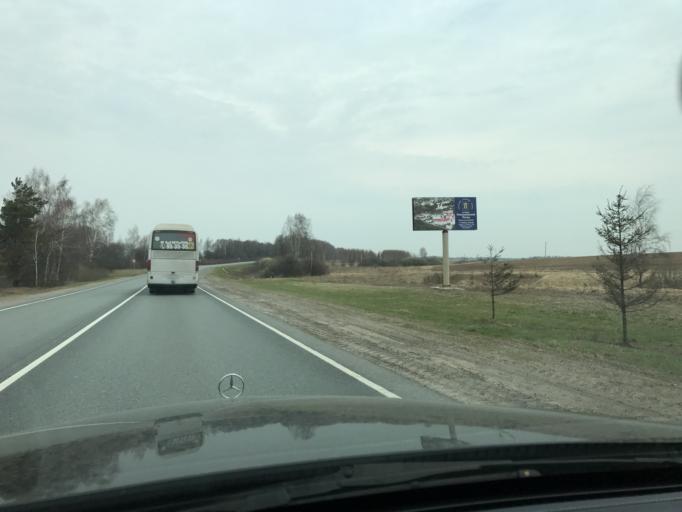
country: RU
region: Vladimir
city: Suzdal'
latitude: 56.3580
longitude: 40.4691
